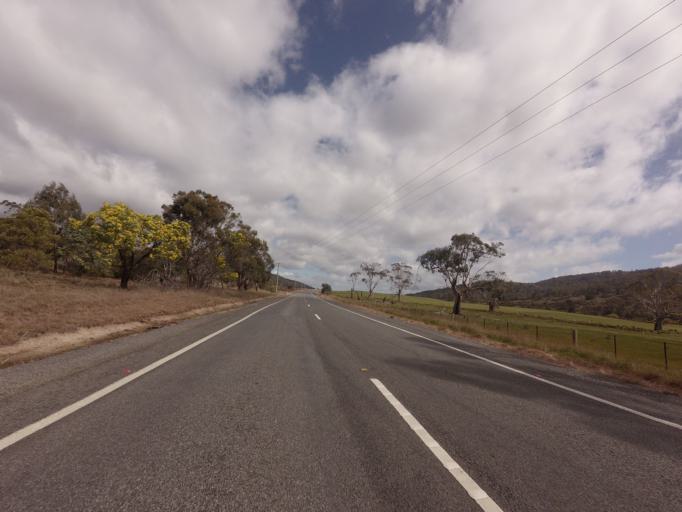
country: AU
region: Tasmania
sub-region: Northern Midlands
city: Evandale
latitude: -41.8112
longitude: 147.5911
